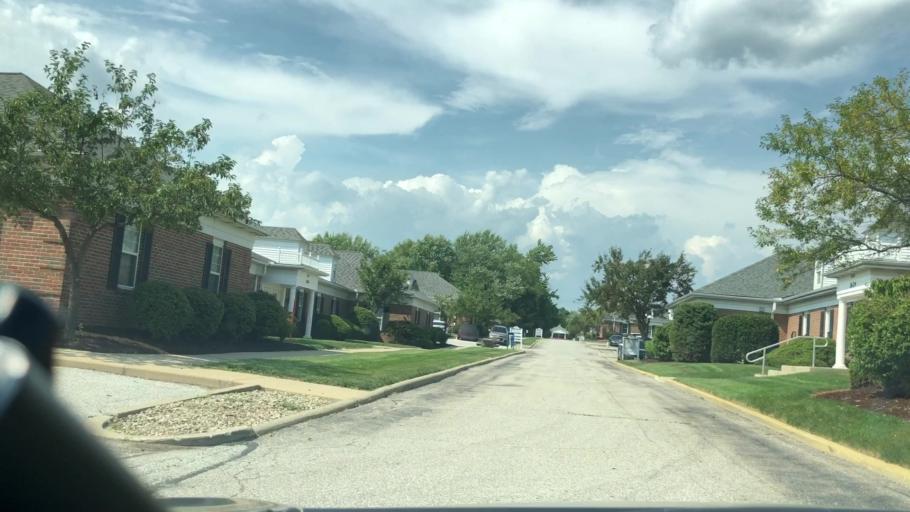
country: US
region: Ohio
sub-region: Summit County
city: Fairlawn
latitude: 41.1327
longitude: -81.6307
